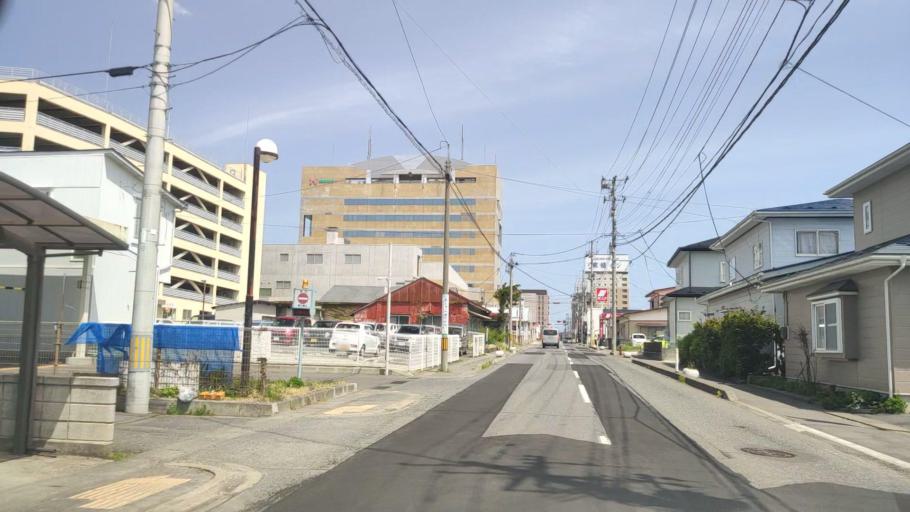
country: JP
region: Aomori
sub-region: Hachinohe Shi
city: Uchimaru
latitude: 40.5070
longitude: 141.4308
